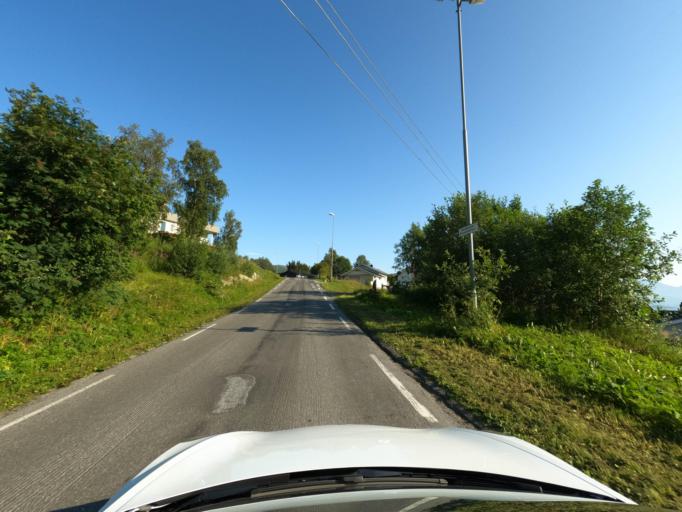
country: NO
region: Nordland
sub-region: Narvik
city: Bjerkvik
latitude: 68.5529
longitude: 17.5602
